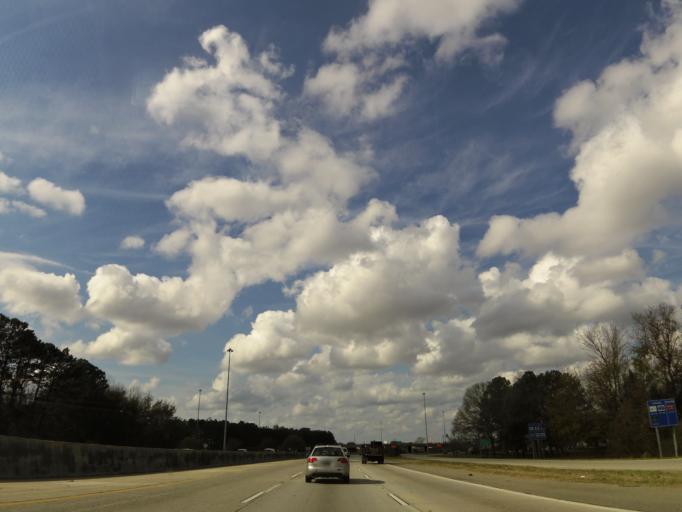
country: US
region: South Carolina
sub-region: Charleston County
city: North Charleston
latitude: 32.8695
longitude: -80.0078
